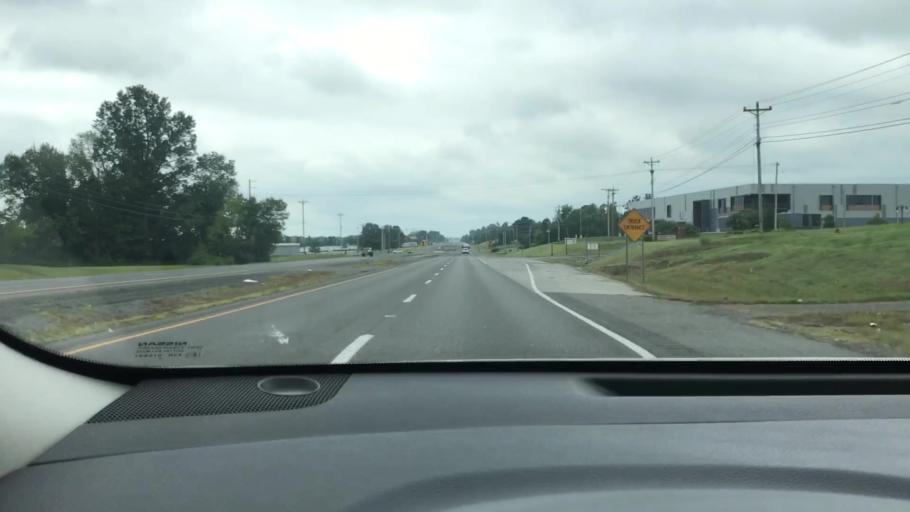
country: US
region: Kentucky
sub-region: Calloway County
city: Murray
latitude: 36.6625
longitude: -88.3053
